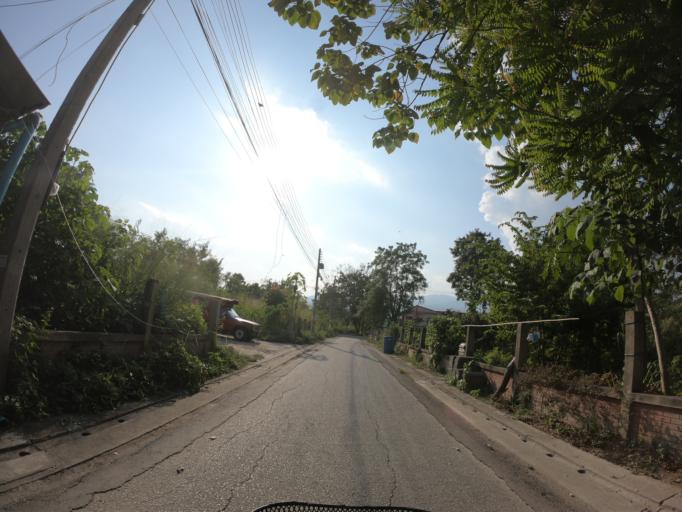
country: TH
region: Chiang Mai
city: Chiang Mai
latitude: 18.8327
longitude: 98.9874
